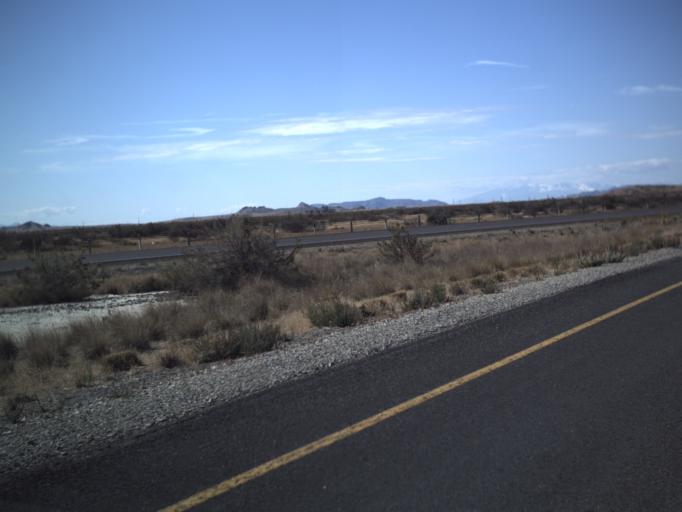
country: US
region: Utah
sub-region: Tooele County
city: Grantsville
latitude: 40.7317
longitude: -113.1181
